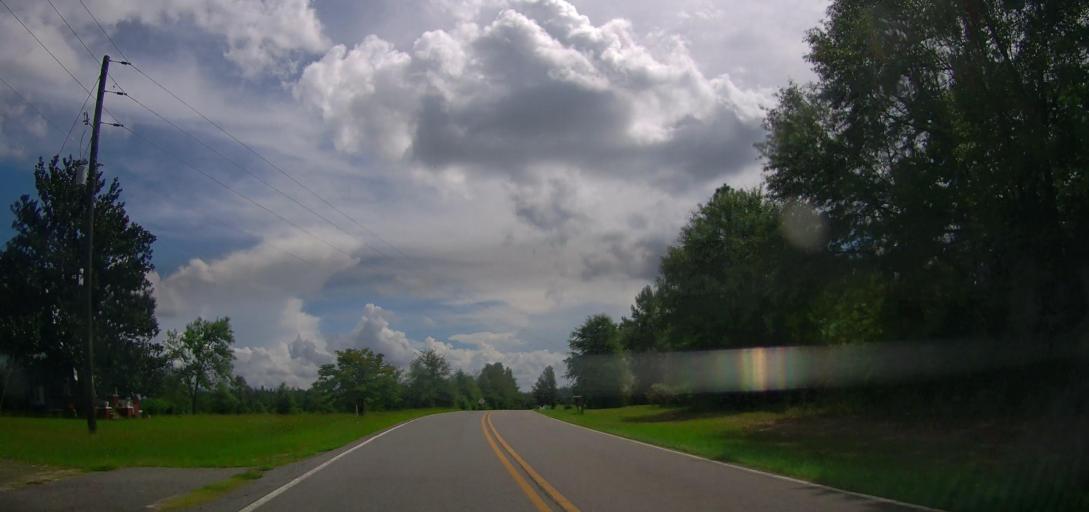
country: US
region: Georgia
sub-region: Taylor County
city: Butler
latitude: 32.4573
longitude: -84.1958
